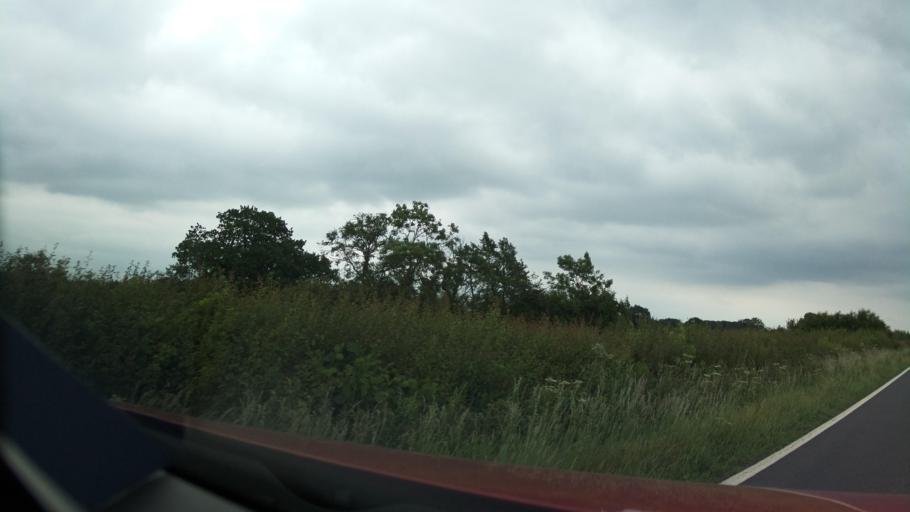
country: GB
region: England
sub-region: Staffordshire
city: Mayfield
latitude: 52.9626
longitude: -1.7578
